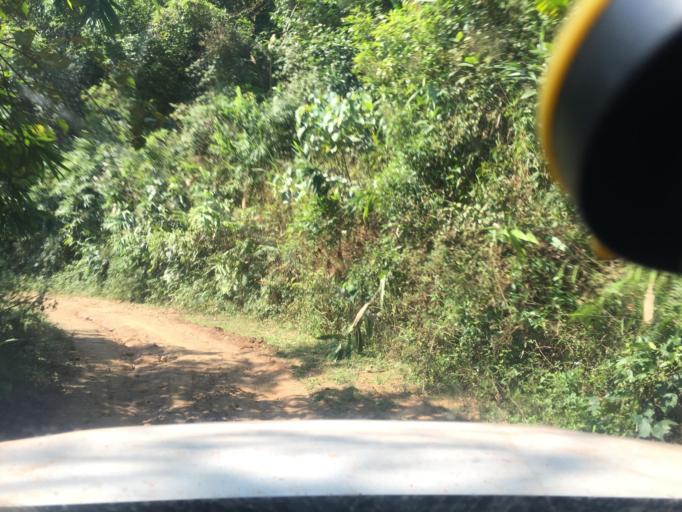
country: LA
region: Phongsali
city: Phongsali
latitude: 21.7045
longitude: 102.3924
